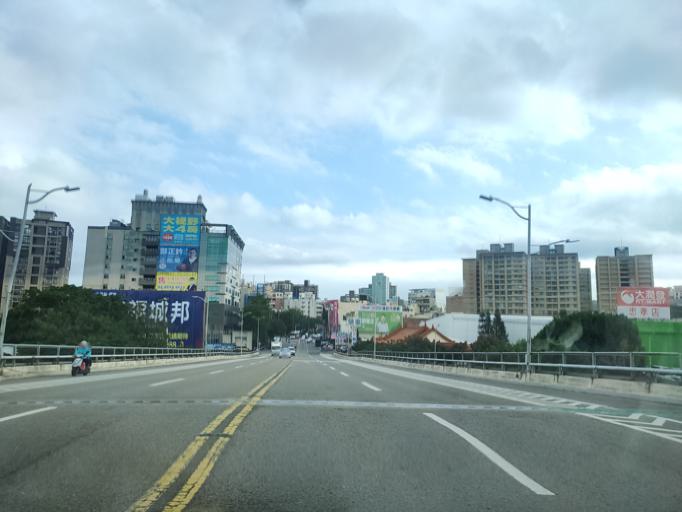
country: TW
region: Taiwan
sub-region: Hsinchu
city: Hsinchu
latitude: 24.8076
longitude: 120.9850
